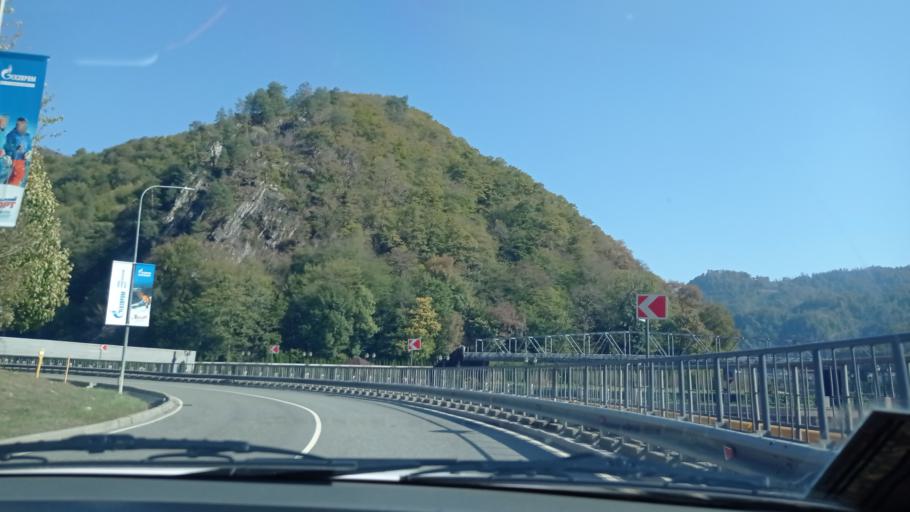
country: RU
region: Krasnodarskiy
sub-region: Sochi City
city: Krasnaya Polyana
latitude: 43.6807
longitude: 40.2760
